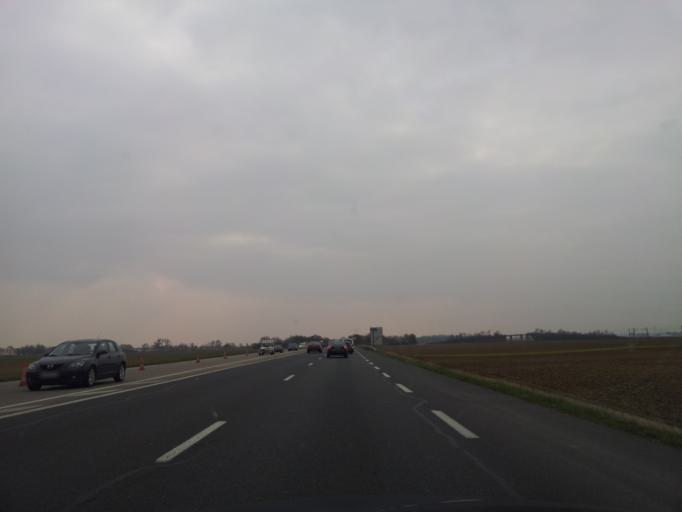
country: FR
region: Alsace
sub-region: Departement du Bas-Rhin
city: Lipsheim
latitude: 48.4841
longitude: 7.6728
